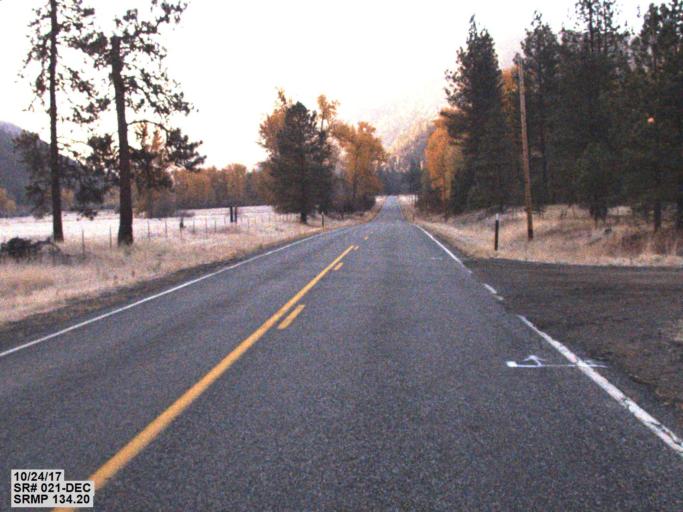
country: US
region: Washington
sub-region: Ferry County
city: Republic
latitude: 48.3094
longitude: -118.7381
